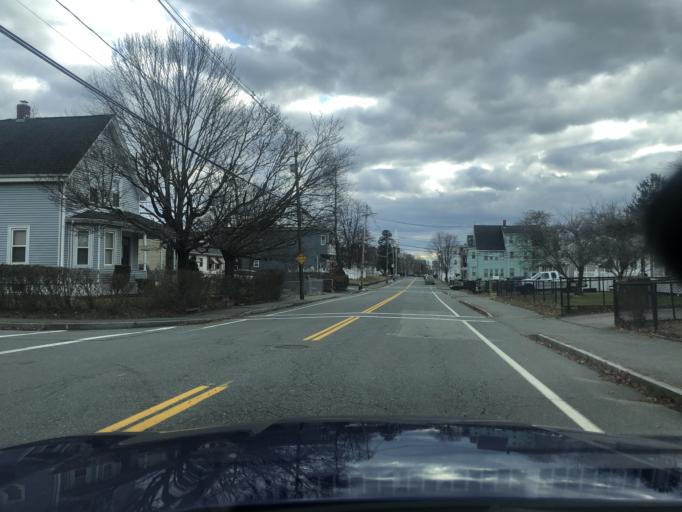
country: US
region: Massachusetts
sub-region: Plymouth County
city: Brockton
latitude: 42.1048
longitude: -71.0134
